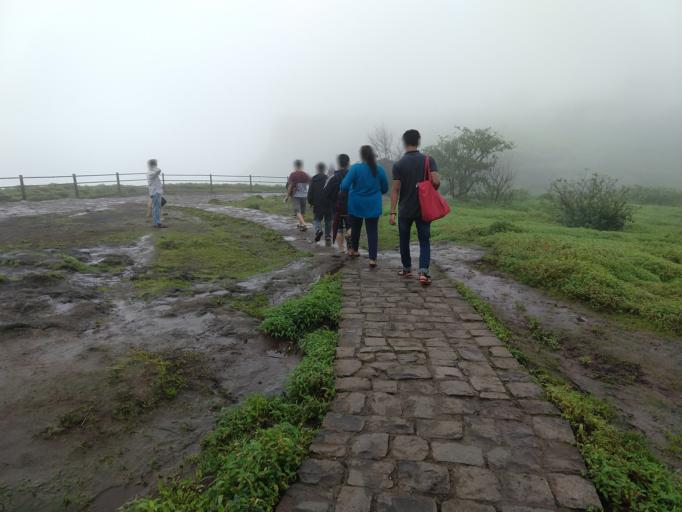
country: IN
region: Maharashtra
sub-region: Pune Division
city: Kharakvasla
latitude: 18.3653
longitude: 73.7533
